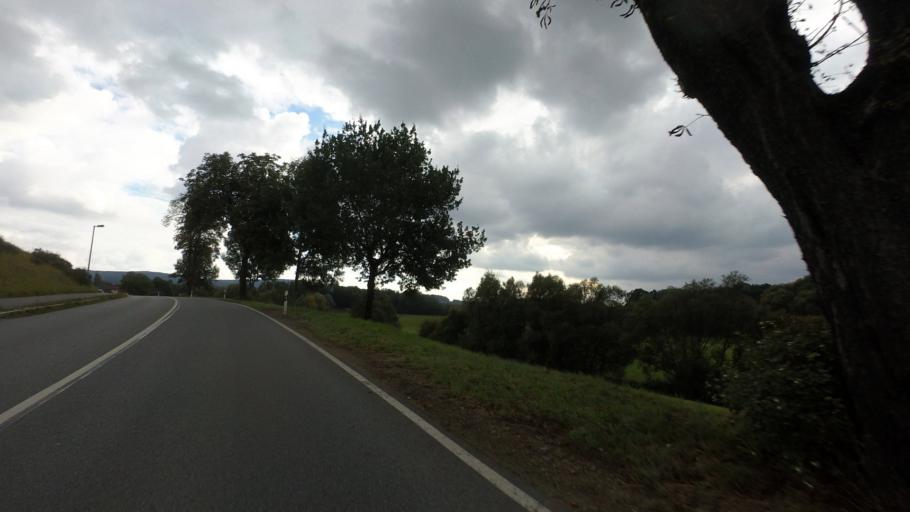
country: DE
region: Saxony
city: Grosspostwitz
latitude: 51.1093
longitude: 14.4567
